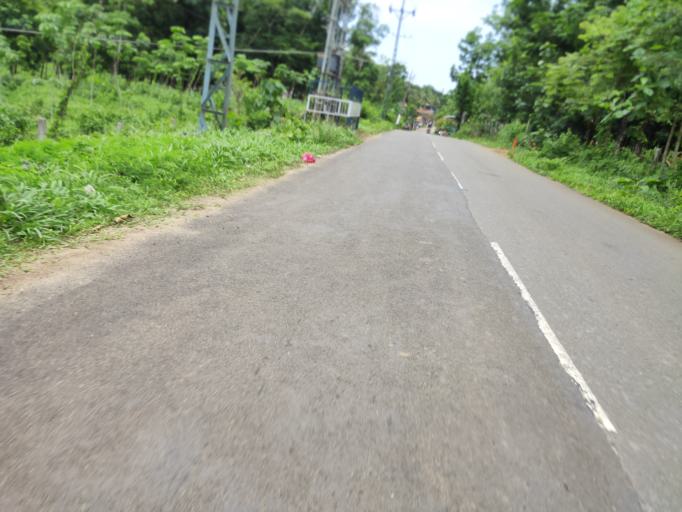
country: IN
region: Kerala
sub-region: Malappuram
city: Manjeri
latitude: 11.2174
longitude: 76.2609
